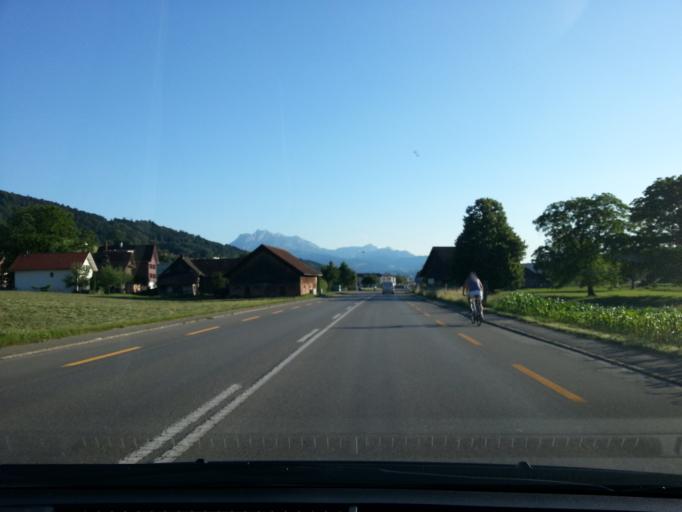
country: CH
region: Lucerne
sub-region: Lucerne-Land District
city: Root
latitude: 47.1008
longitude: 8.3727
